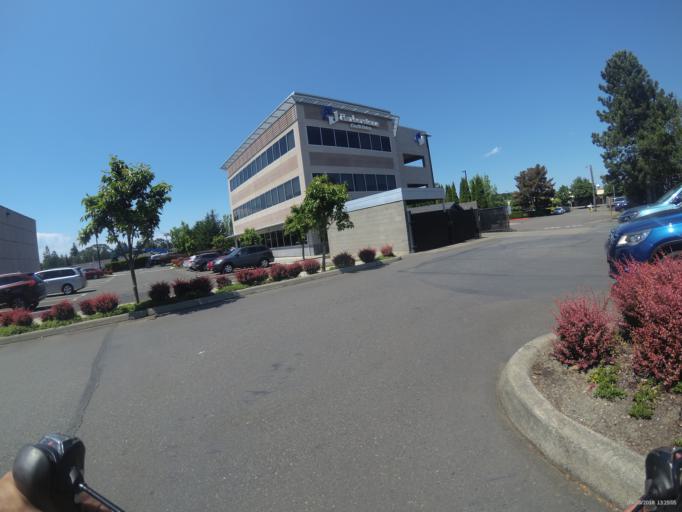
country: US
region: Washington
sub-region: Pierce County
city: Lakewood
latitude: 47.1686
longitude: -122.5177
